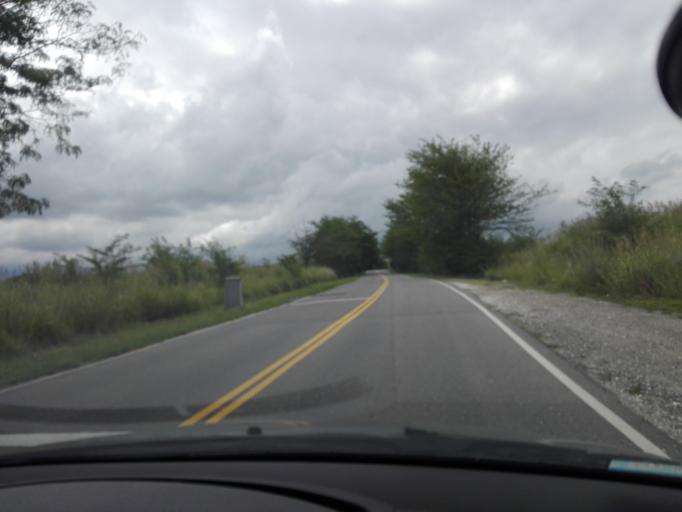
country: AR
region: Cordoba
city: Cuesta Blanca
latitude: -31.6056
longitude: -64.5615
